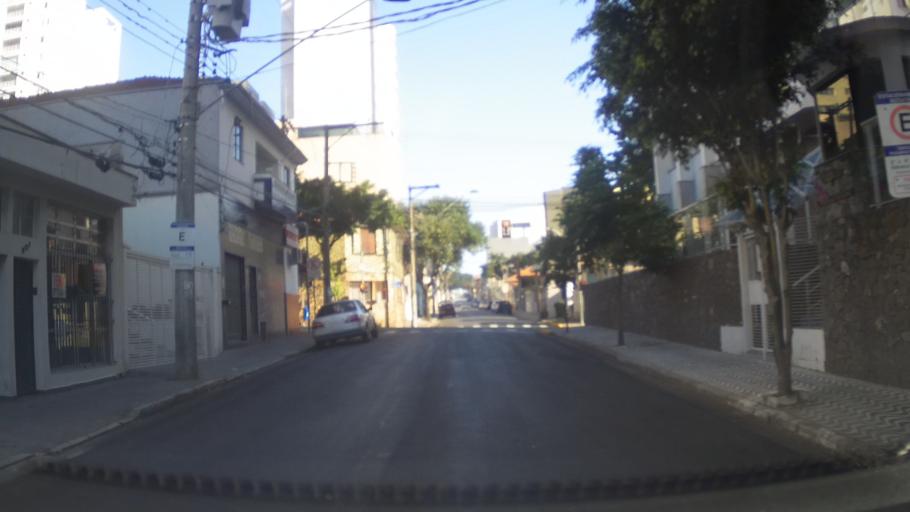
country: BR
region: Sao Paulo
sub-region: Sao Caetano Do Sul
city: Sao Caetano do Sul
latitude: -23.6217
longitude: -46.5657
